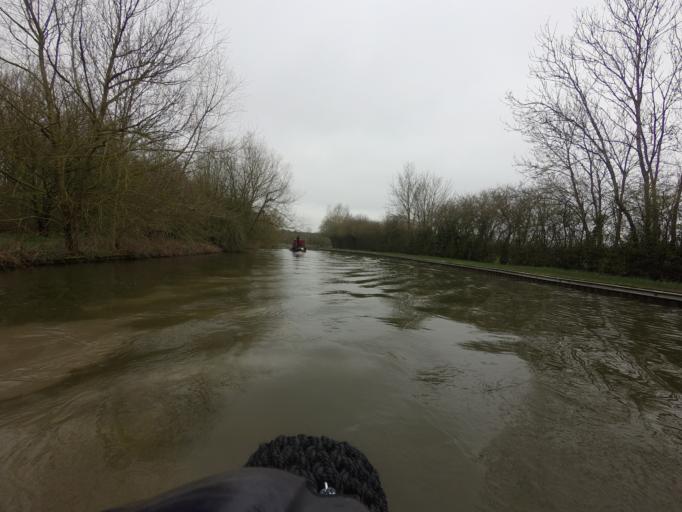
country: GB
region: England
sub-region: Buckinghamshire
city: Cheddington
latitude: 51.8428
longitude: -0.6502
